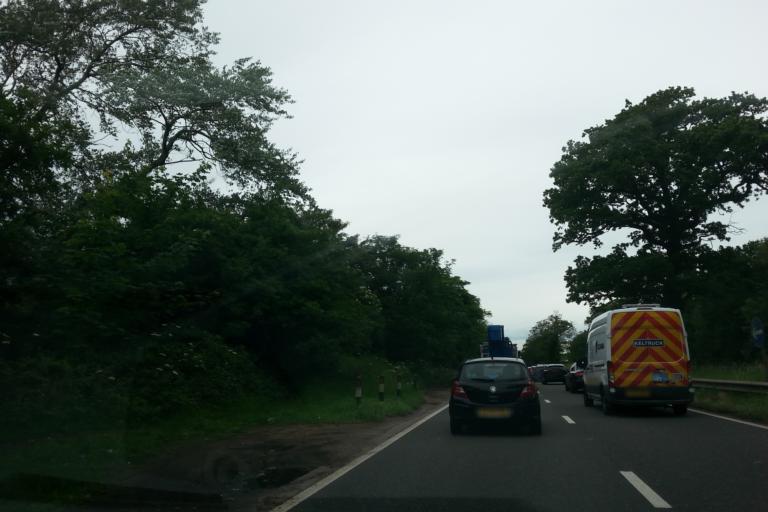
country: GB
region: England
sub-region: Solihull
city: Bickenhill
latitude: 52.4637
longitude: -1.7038
